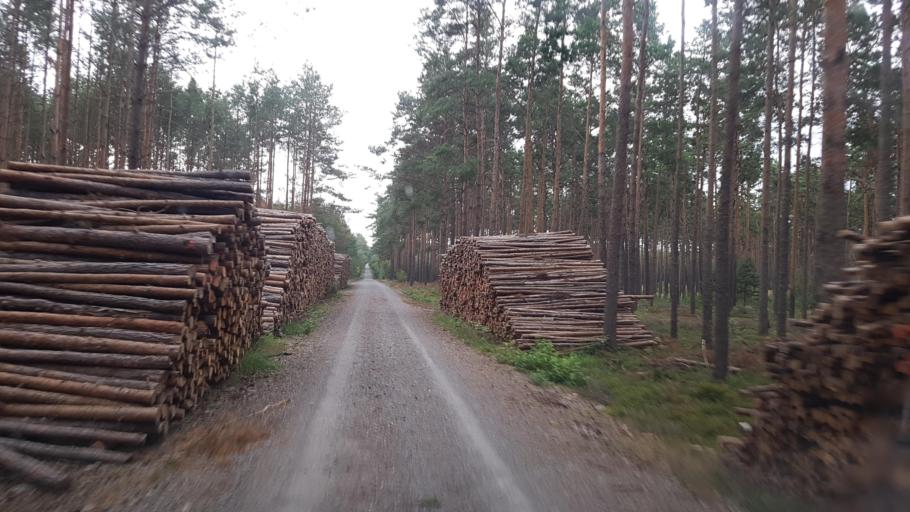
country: DE
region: Brandenburg
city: Schonborn
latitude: 51.6145
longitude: 13.4964
